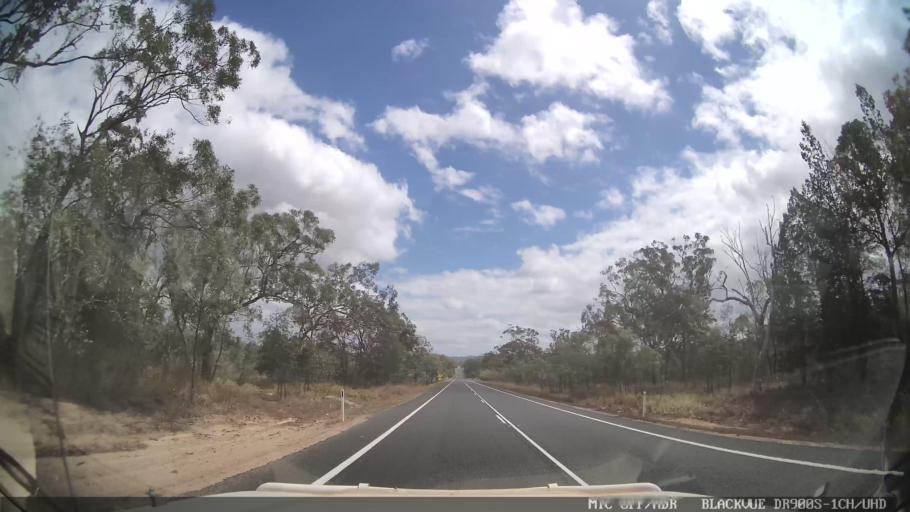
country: AU
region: Queensland
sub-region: Tablelands
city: Ravenshoe
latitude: -17.6517
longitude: 145.3201
